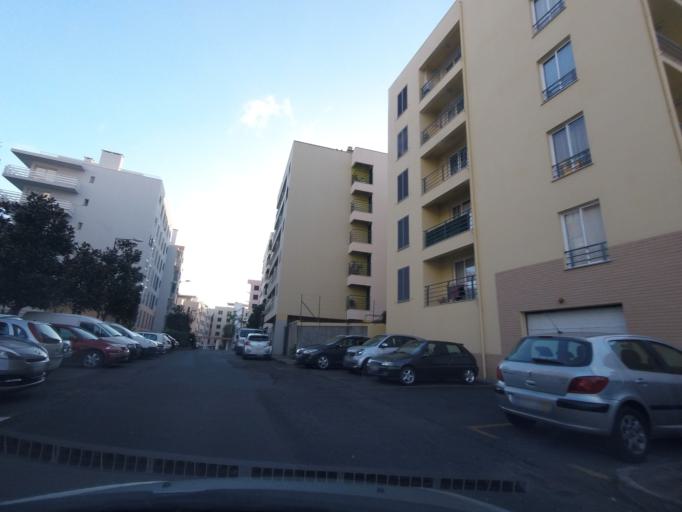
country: PT
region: Madeira
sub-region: Funchal
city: Nossa Senhora do Monte
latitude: 32.6556
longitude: -16.9315
